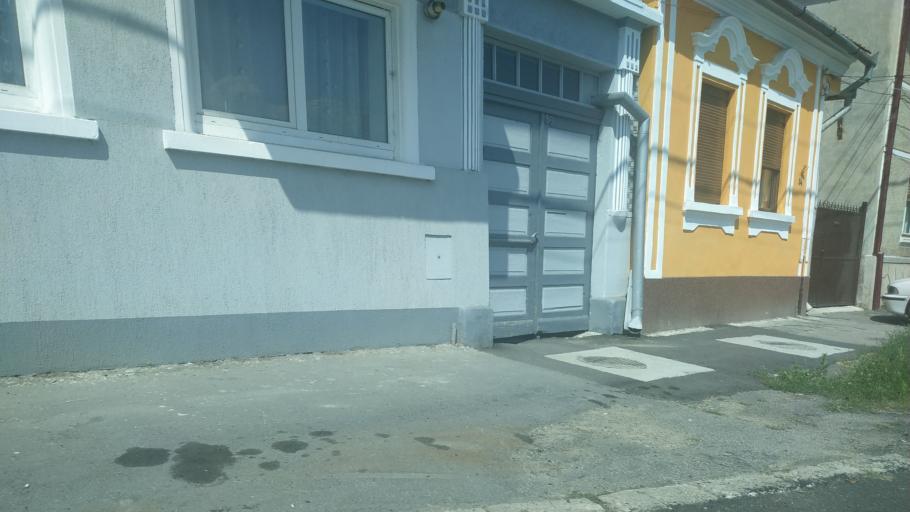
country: RO
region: Brasov
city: Fogarasch
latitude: 45.8420
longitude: 24.9652
